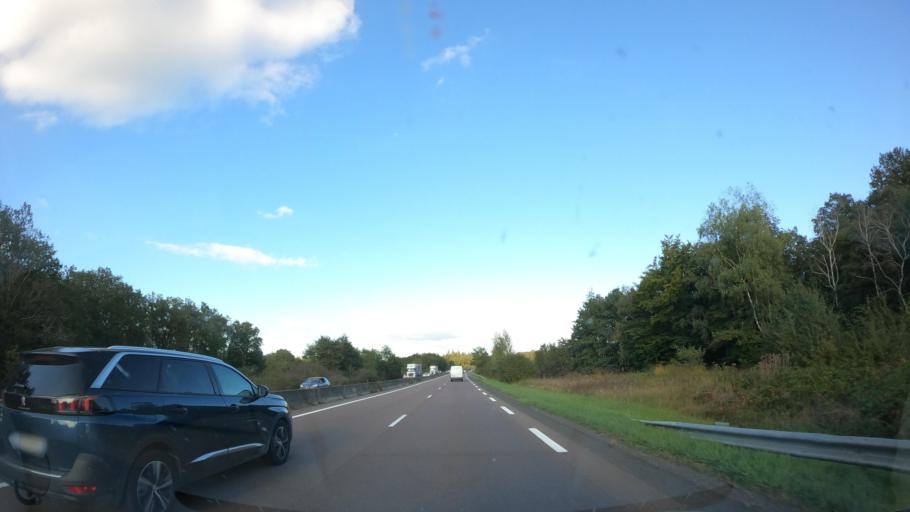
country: FR
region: Bourgogne
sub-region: Departement de Saone-et-Loire
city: Ciry-le-Noble
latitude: 46.6278
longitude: 4.3078
